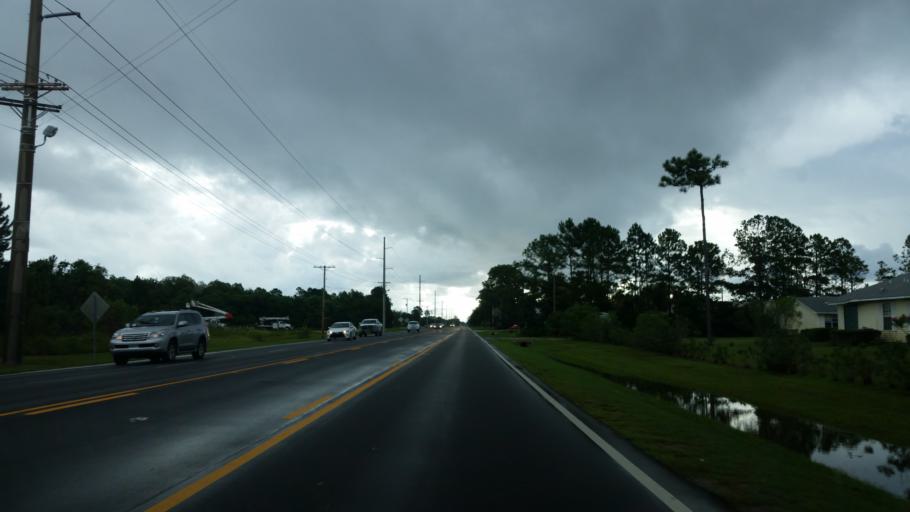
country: US
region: Alabama
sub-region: Baldwin County
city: Orange Beach
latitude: 30.2902
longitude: -87.6141
